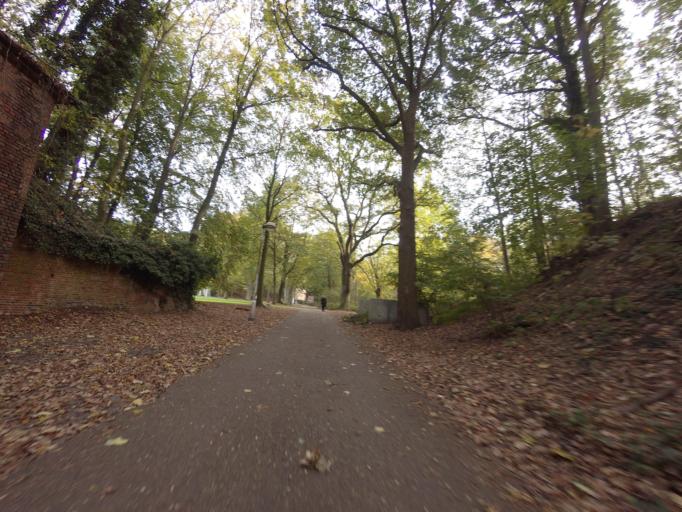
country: BE
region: Flanders
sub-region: Provincie Antwerpen
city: Brasschaat
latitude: 51.2631
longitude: 4.4574
